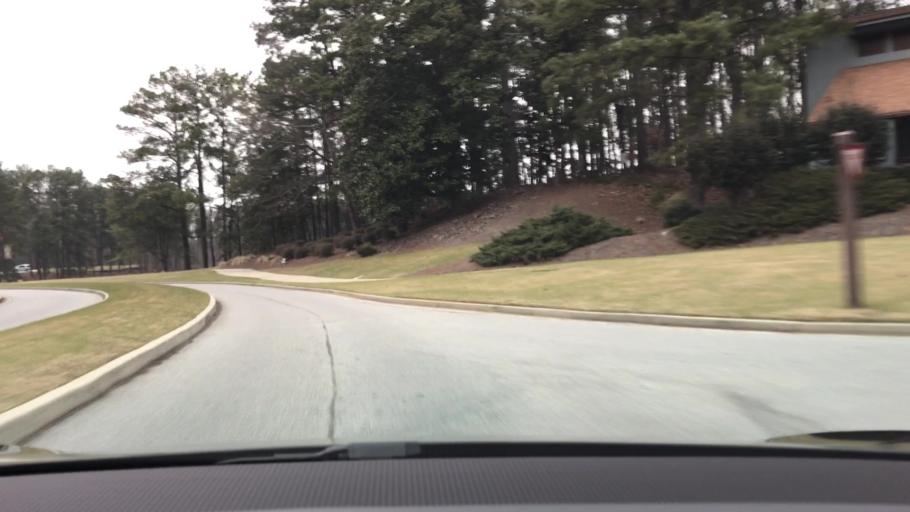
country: US
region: Georgia
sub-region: Gwinnett County
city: Buford
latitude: 34.1720
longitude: -84.0071
